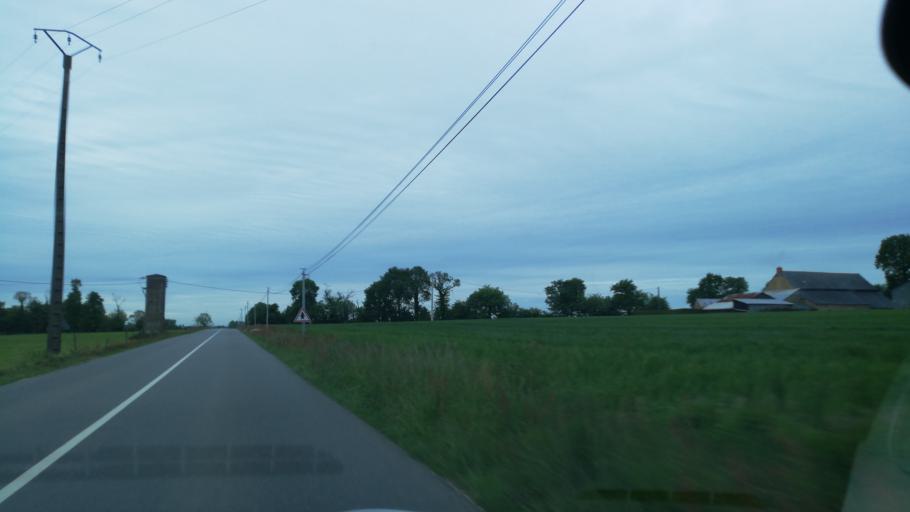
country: FR
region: Brittany
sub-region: Departement d'Ille-et-Vilaine
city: Irodouer
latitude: 48.2170
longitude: -1.9432
